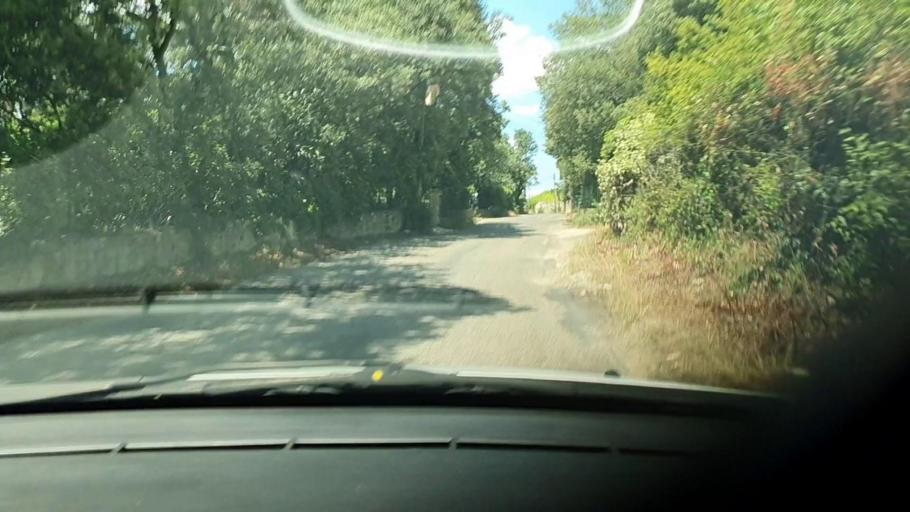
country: FR
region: Languedoc-Roussillon
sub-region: Departement du Gard
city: Montaren-et-Saint-Mediers
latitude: 44.0064
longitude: 4.3902
